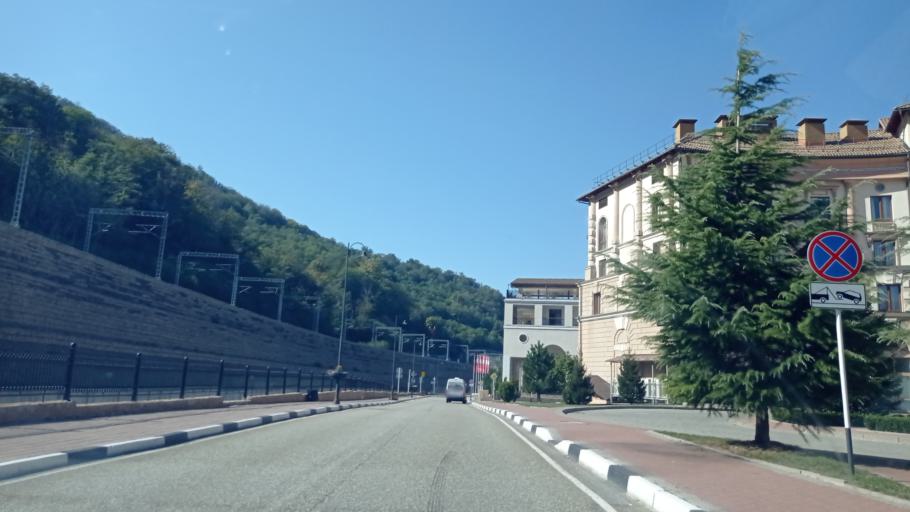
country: RU
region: Krasnodarskiy
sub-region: Sochi City
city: Krasnaya Polyana
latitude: 43.6826
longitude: 40.2590
